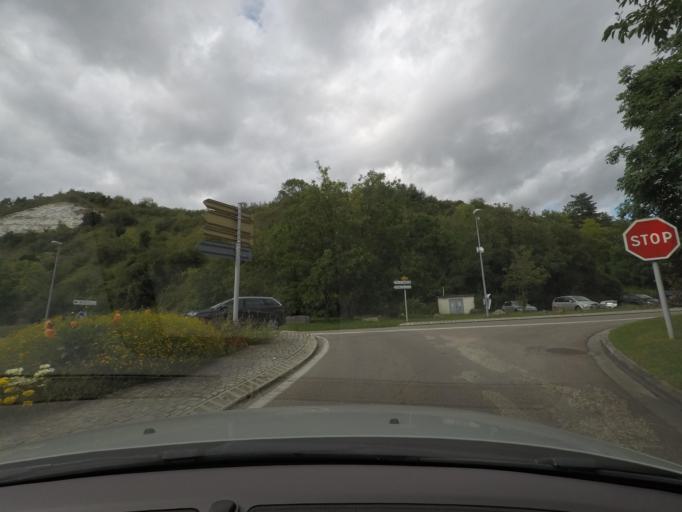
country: FR
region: Haute-Normandie
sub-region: Departement de l'Eure
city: Les Andelys
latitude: 49.2456
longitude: 1.3970
